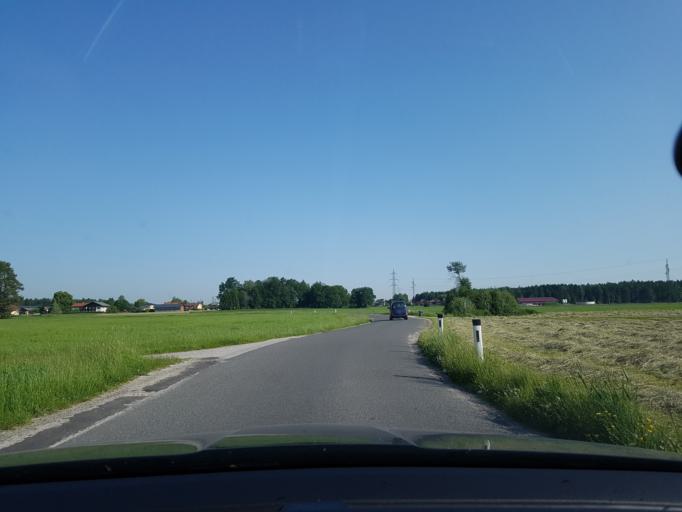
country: AT
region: Salzburg
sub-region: Politischer Bezirk Salzburg-Umgebung
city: Grodig
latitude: 47.7671
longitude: 12.9970
